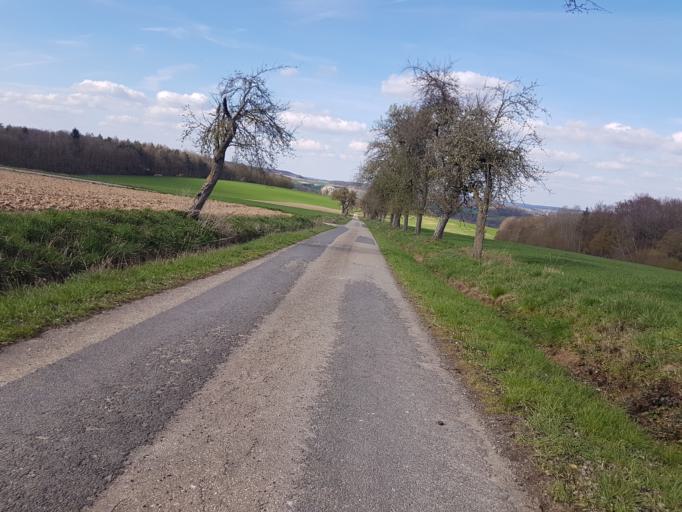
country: DE
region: Baden-Wuerttemberg
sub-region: Regierungsbezirk Stuttgart
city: Forchtenberg
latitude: 49.3305
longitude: 9.5276
